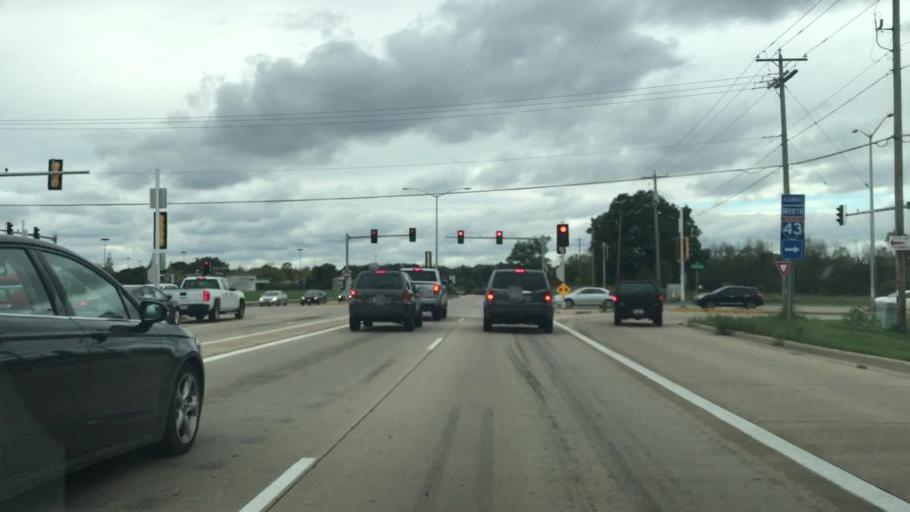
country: US
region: Wisconsin
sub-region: Waukesha County
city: Mukwonago
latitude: 42.8535
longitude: -88.3237
